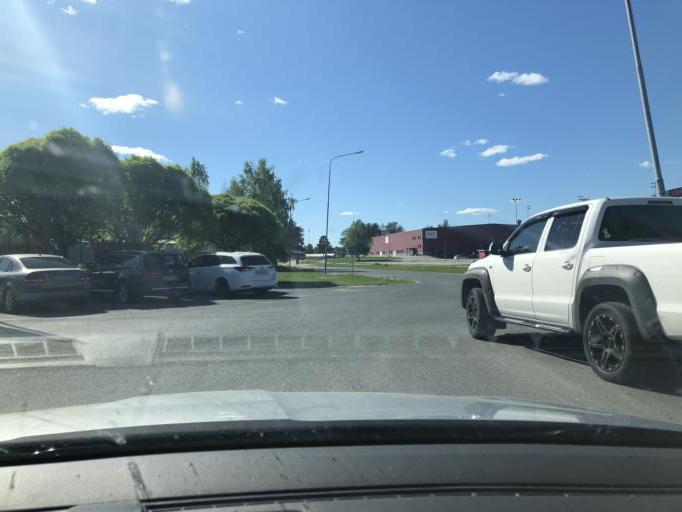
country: SE
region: Norrbotten
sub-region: Kalix Kommun
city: Kalix
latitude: 65.8534
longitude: 23.1836
